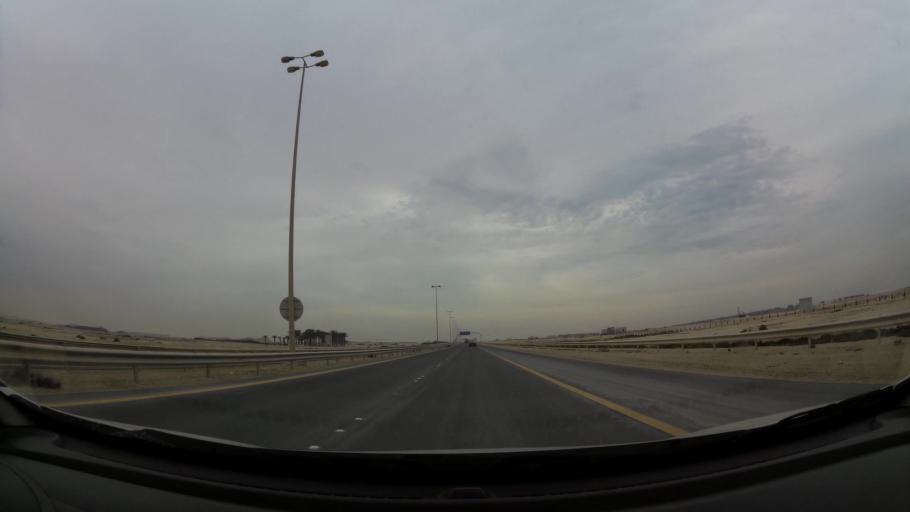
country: BH
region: Central Governorate
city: Dar Kulayb
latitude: 26.0317
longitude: 50.6078
